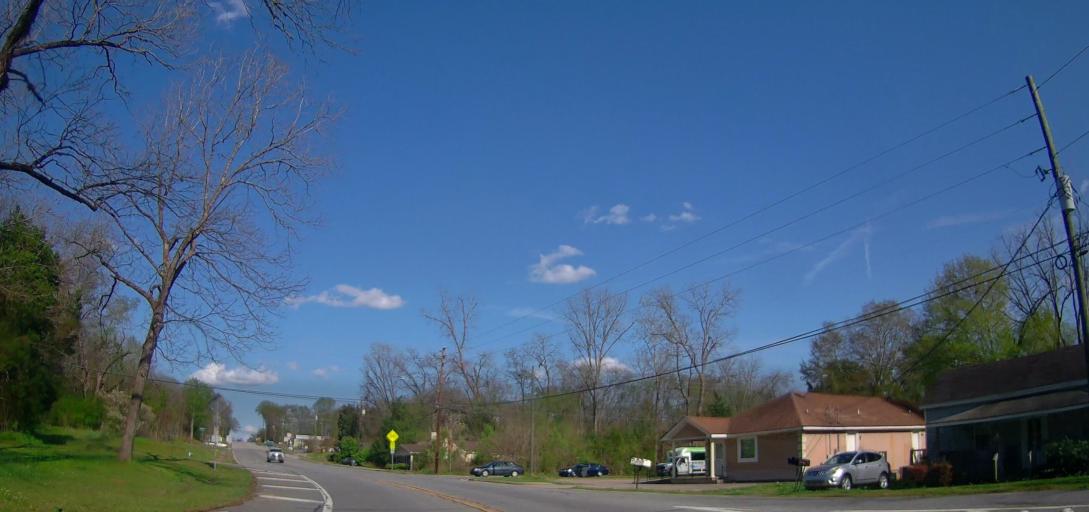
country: US
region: Georgia
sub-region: Baldwin County
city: Milledgeville
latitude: 33.0811
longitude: -83.2434
